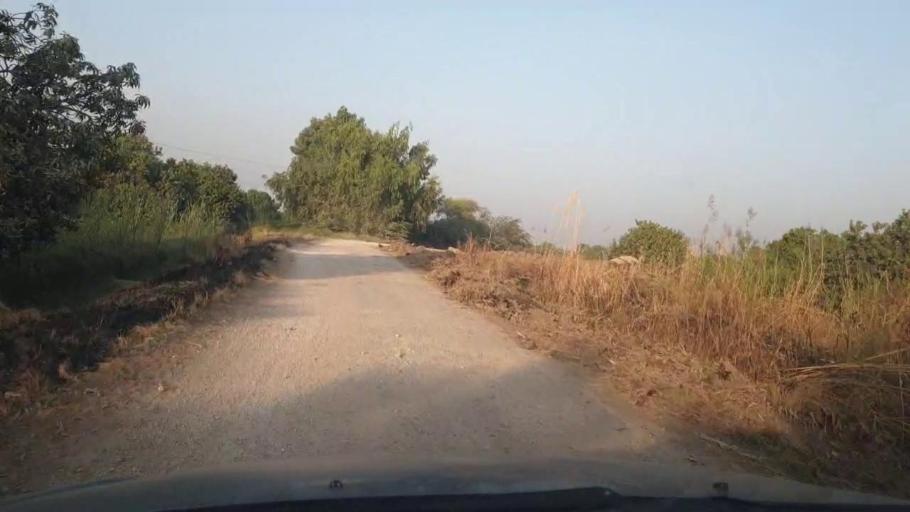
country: PK
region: Sindh
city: Tando Jam
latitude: 25.4262
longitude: 68.4961
